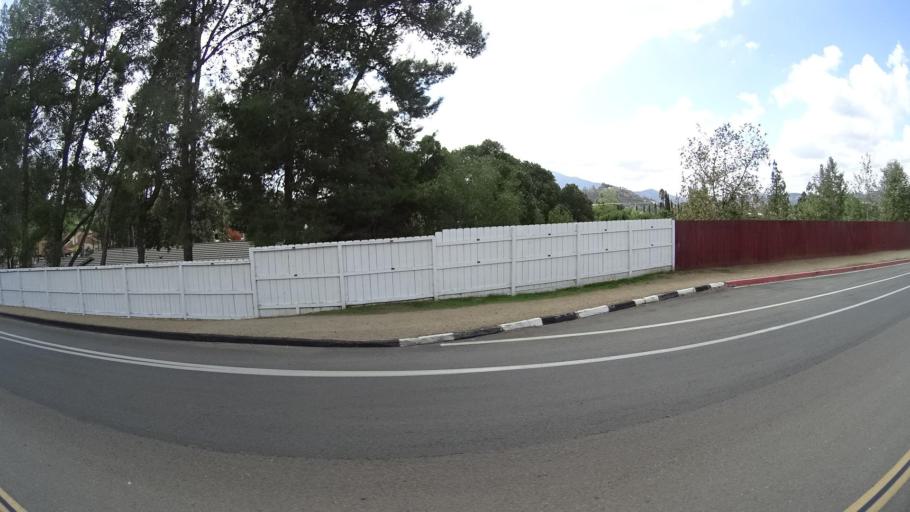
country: US
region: California
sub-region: San Diego County
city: Rancho San Diego
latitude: 32.7621
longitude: -116.9169
